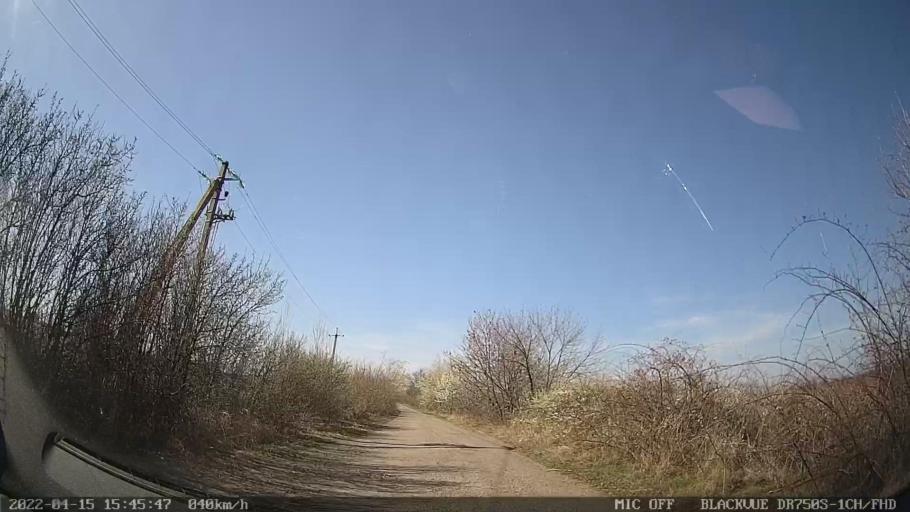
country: MD
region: Raionul Ocnita
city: Otaci
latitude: 48.3781
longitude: 27.9170
